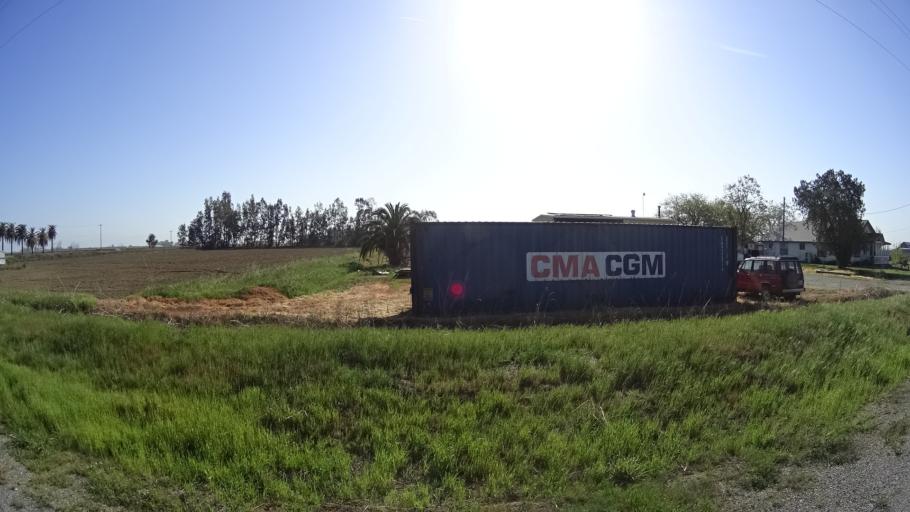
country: US
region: California
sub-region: Glenn County
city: Willows
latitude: 39.5807
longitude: -122.1076
